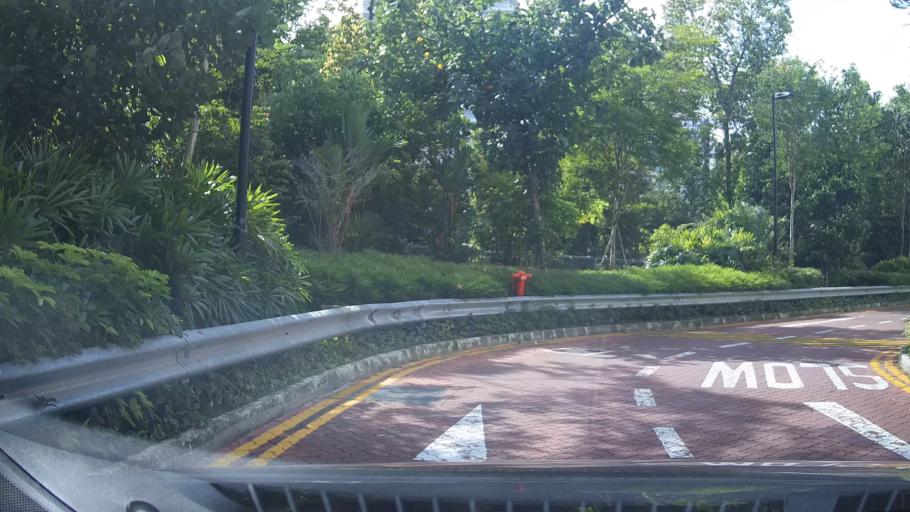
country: SG
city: Singapore
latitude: 1.3282
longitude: 103.8614
